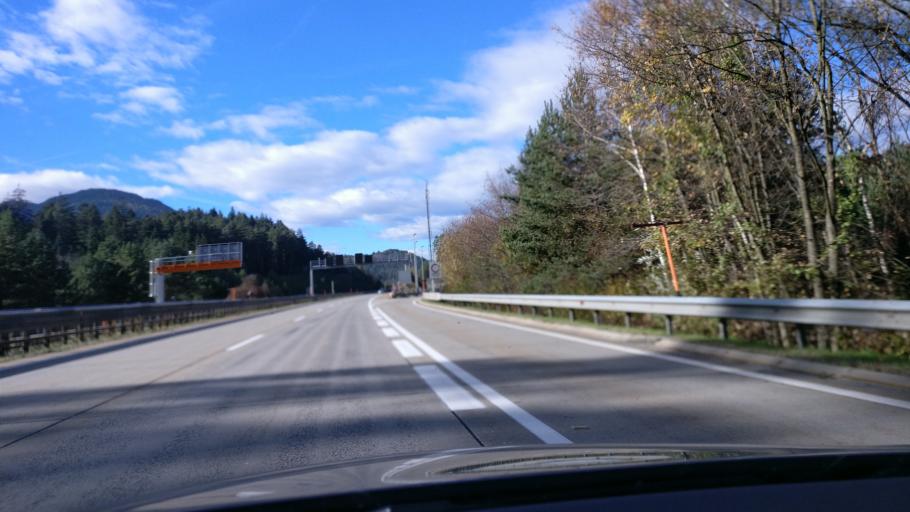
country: AT
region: Carinthia
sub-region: Politischer Bezirk Villach Land
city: Fresach
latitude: 46.6531
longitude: 13.7422
